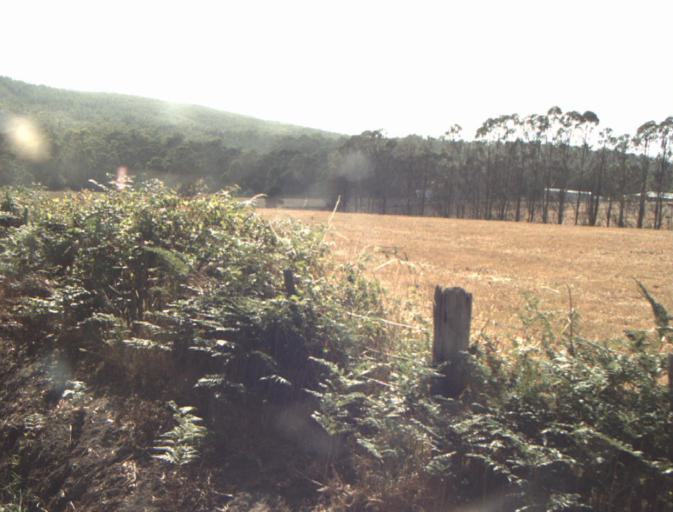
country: AU
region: Tasmania
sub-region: Dorset
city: Bridport
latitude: -41.1527
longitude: 147.2278
